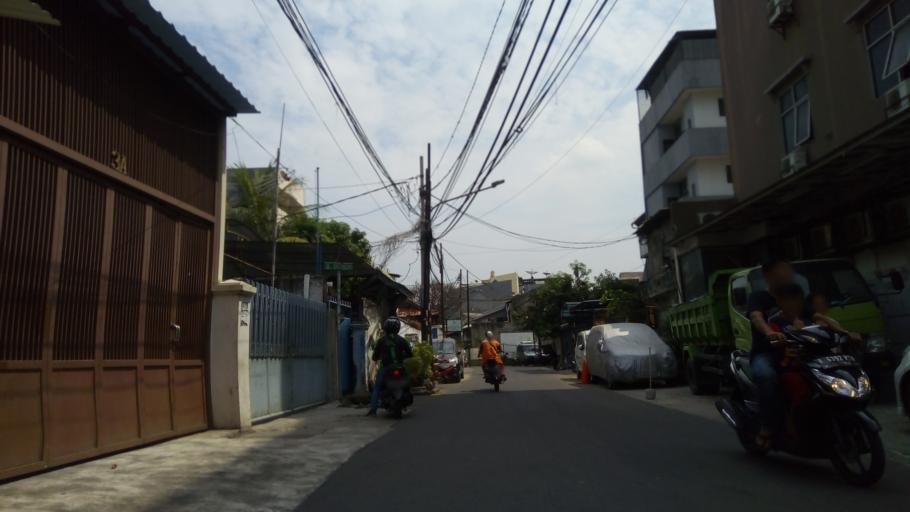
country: ID
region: Jakarta Raya
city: Jakarta
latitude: -6.1513
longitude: 106.8303
